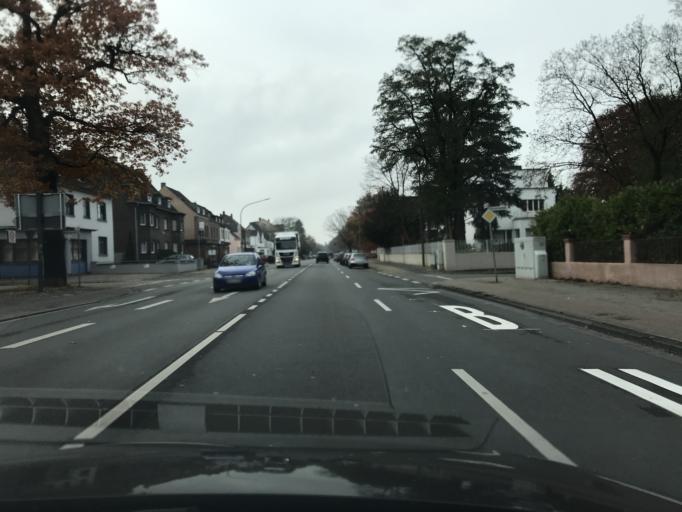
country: DE
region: North Rhine-Westphalia
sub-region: Regierungsbezirk Arnsberg
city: Hamm
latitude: 51.6914
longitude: 7.8565
